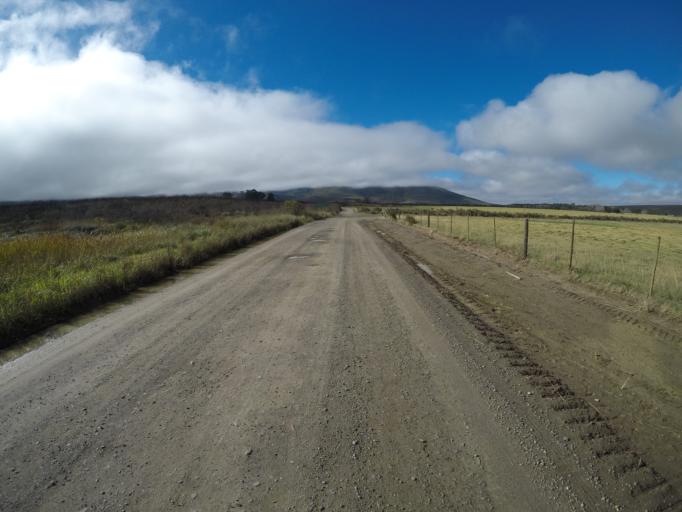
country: ZA
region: Western Cape
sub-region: Cape Winelands District Municipality
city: Ashton
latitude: -34.1222
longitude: 19.8374
